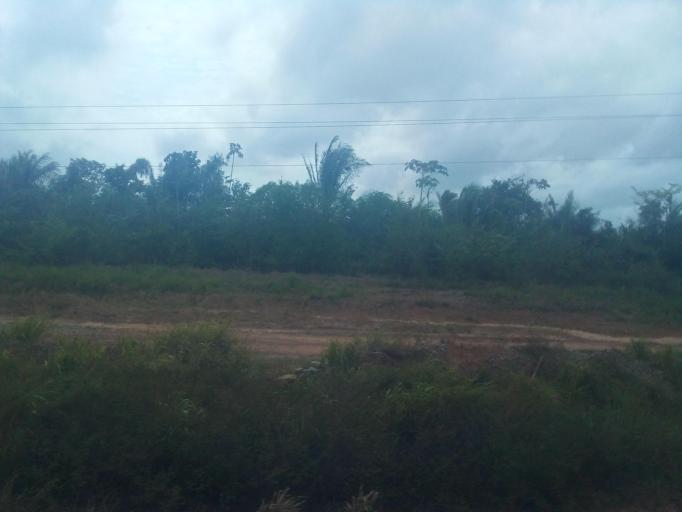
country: BR
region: Maranhao
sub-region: Itapecuru Mirim
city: Itapecuru Mirim
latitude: -3.1702
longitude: -44.3622
